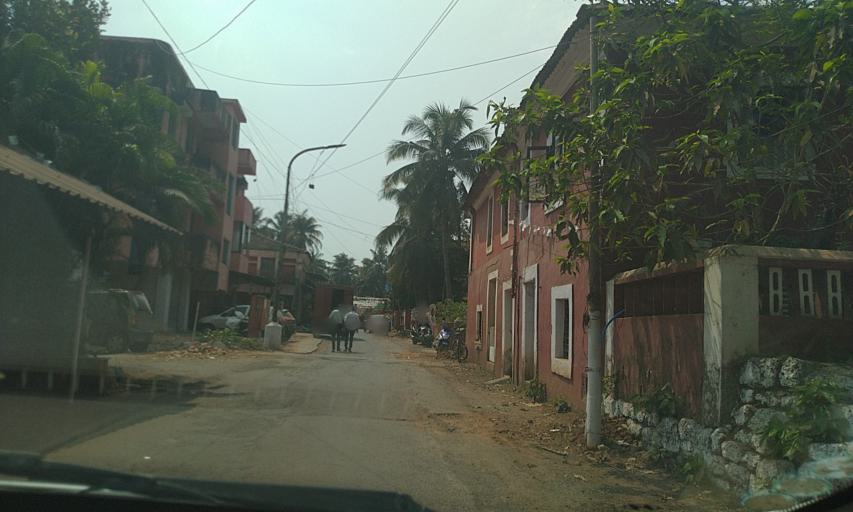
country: IN
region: Goa
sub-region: North Goa
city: Panaji
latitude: 15.4895
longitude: 73.8308
